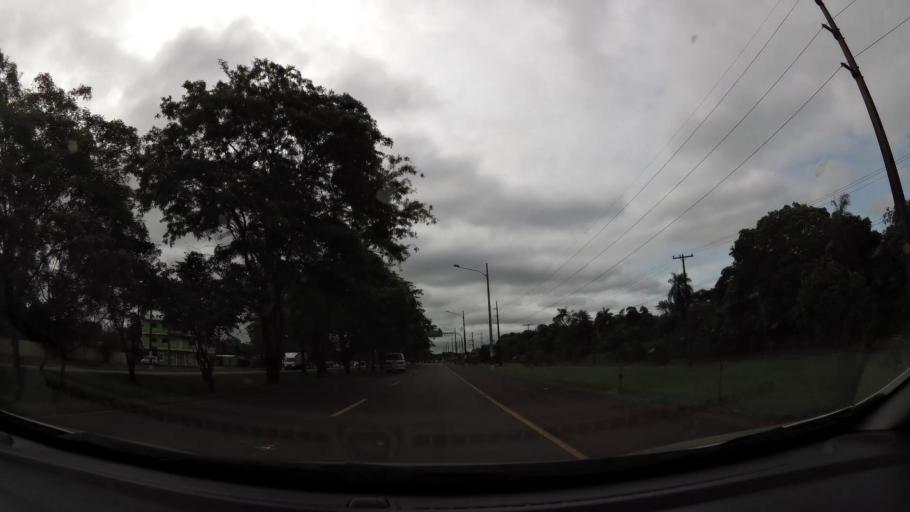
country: PY
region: Alto Parana
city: Ciudad del Este
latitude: -25.4377
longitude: -54.6353
